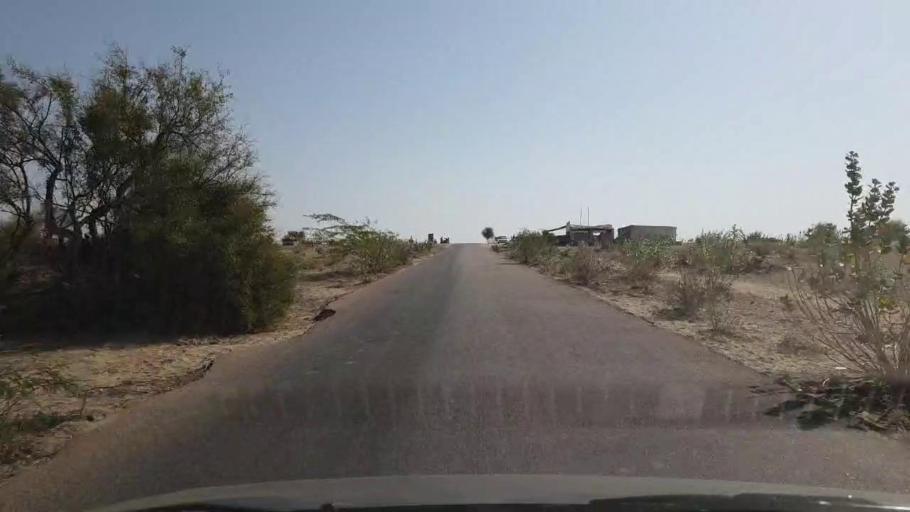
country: PK
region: Sindh
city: Chor
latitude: 25.4878
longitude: 69.7906
